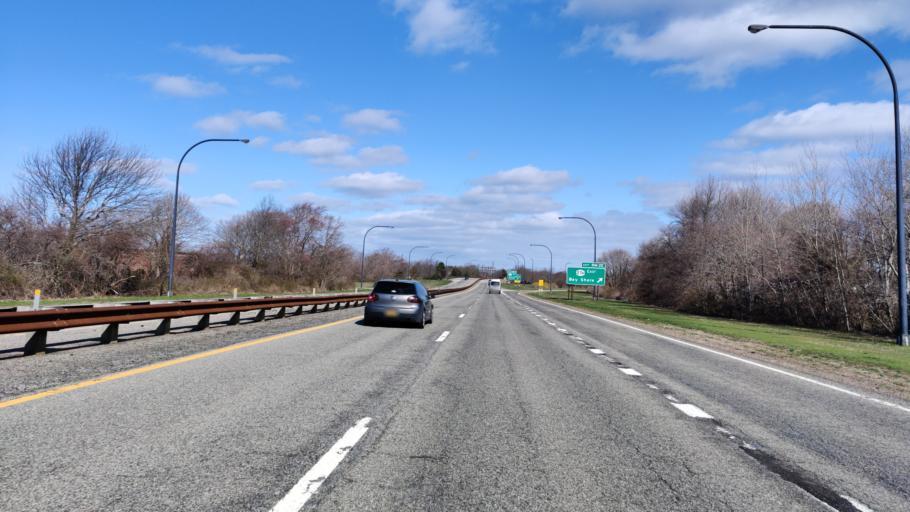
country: US
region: New York
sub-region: Suffolk County
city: West Bay Shore
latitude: 40.6929
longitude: -73.2854
